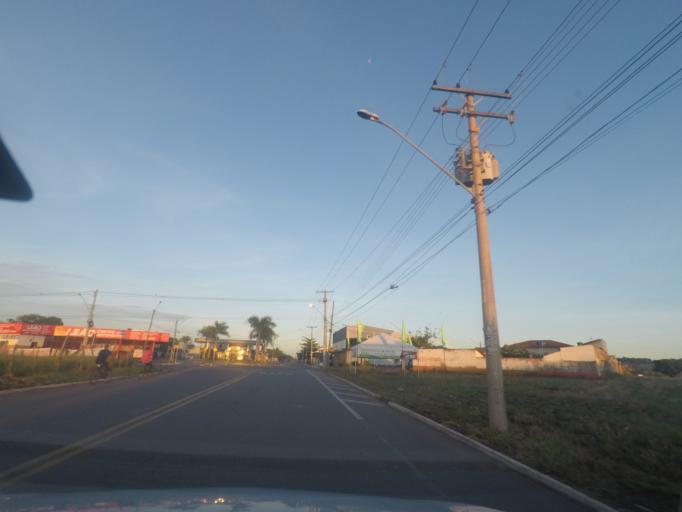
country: BR
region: Goias
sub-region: Goiania
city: Goiania
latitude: -16.6893
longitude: -49.3447
